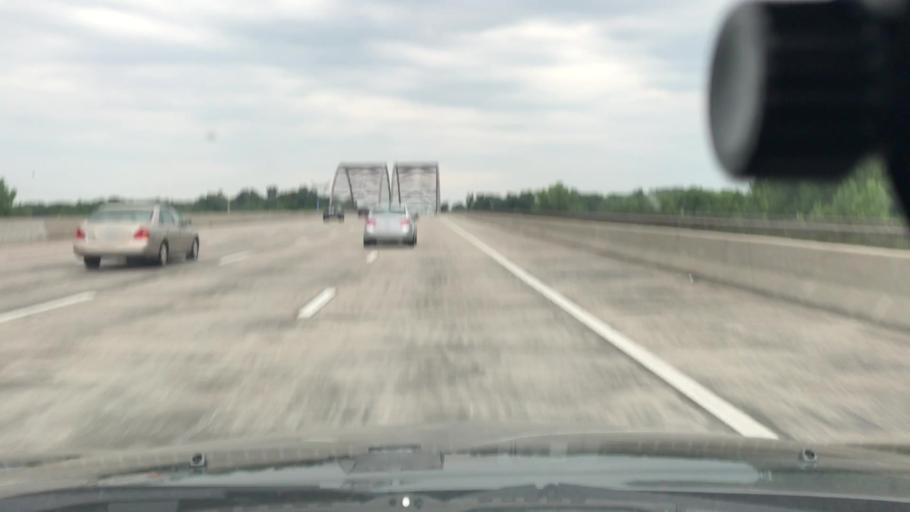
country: US
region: Missouri
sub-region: Saint Charles County
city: Saint Charles
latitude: 38.7329
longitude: -90.5190
